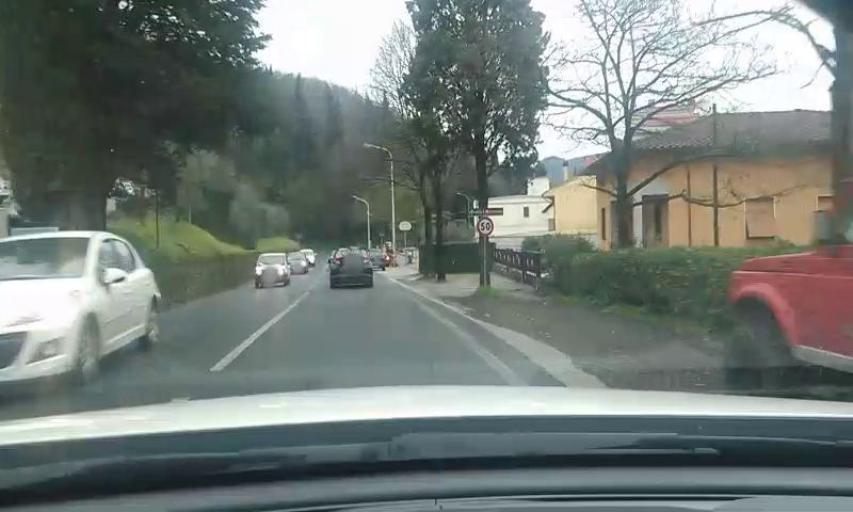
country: IT
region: Tuscany
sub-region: Provincia di Prato
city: Vaiano
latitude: 43.9477
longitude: 11.1251
